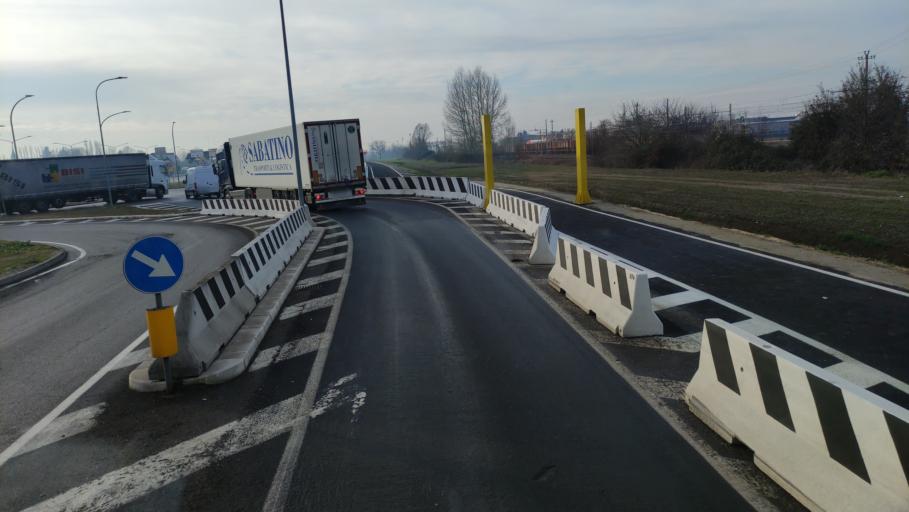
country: IT
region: Emilia-Romagna
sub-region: Provincia di Bologna
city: San Giorgio di Piano
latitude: 44.6125
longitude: 11.3747
